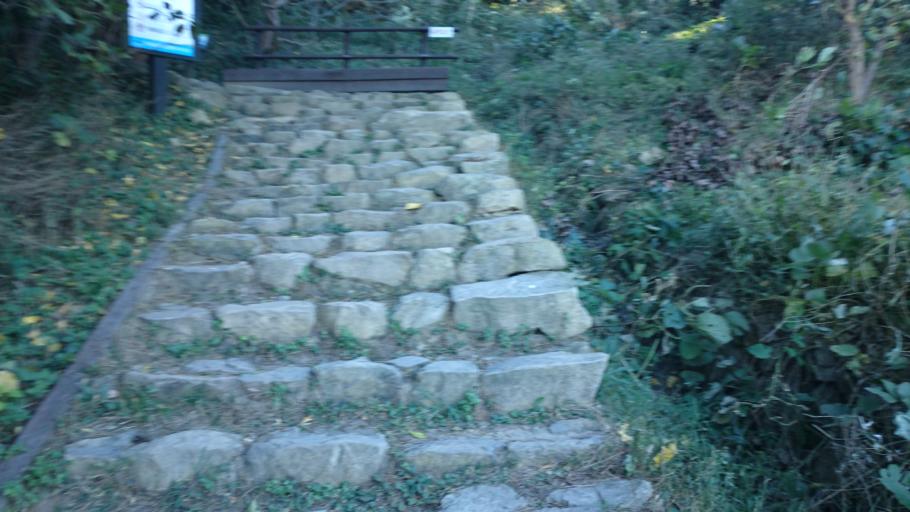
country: KR
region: Gyeongsangnam-do
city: Kyosai
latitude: 34.6274
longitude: 128.5505
